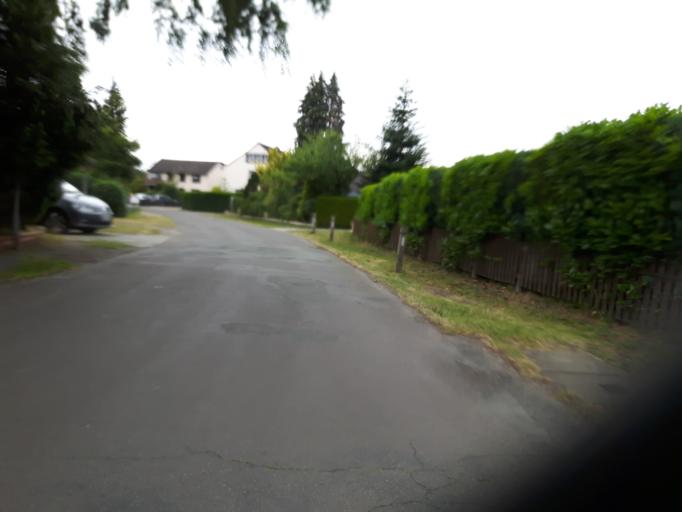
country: DE
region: Lower Saxony
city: Stuhr
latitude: 53.0299
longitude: 8.7331
